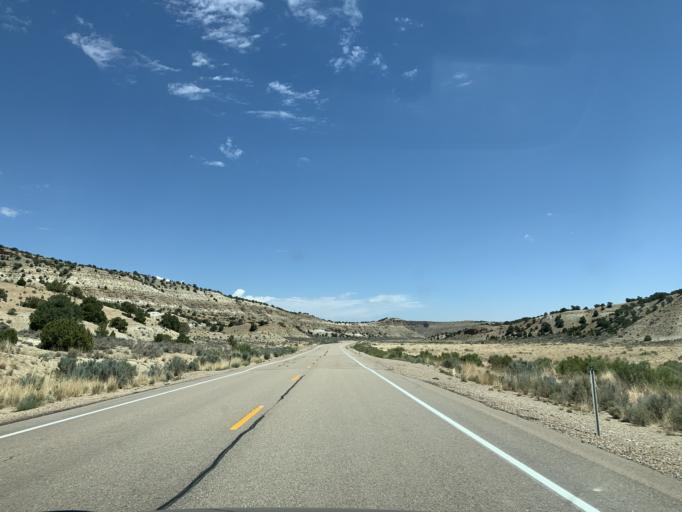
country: US
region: Utah
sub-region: Duchesne County
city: Duchesne
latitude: 39.9651
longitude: -110.1815
